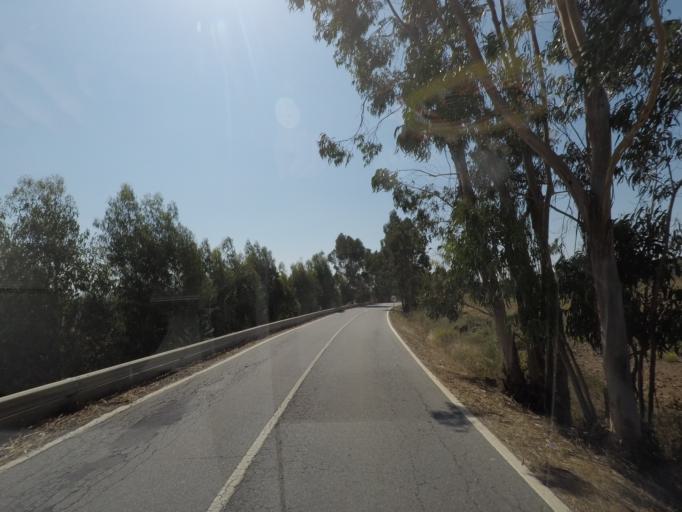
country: PT
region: Beja
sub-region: Odemira
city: Sao Teotonio
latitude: 37.5267
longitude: -8.6998
